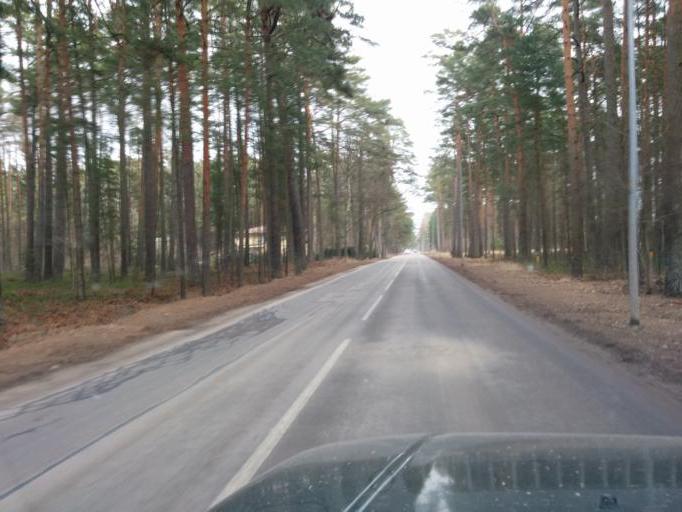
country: LV
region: Jurmala
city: Jurmala
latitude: 56.9455
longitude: 23.7290
